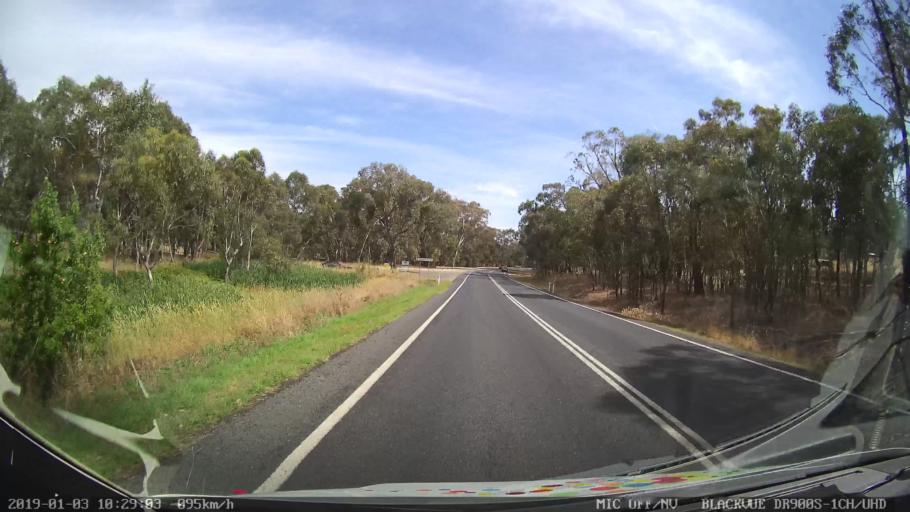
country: AU
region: New South Wales
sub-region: Young
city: Young
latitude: -34.3792
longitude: 148.2599
